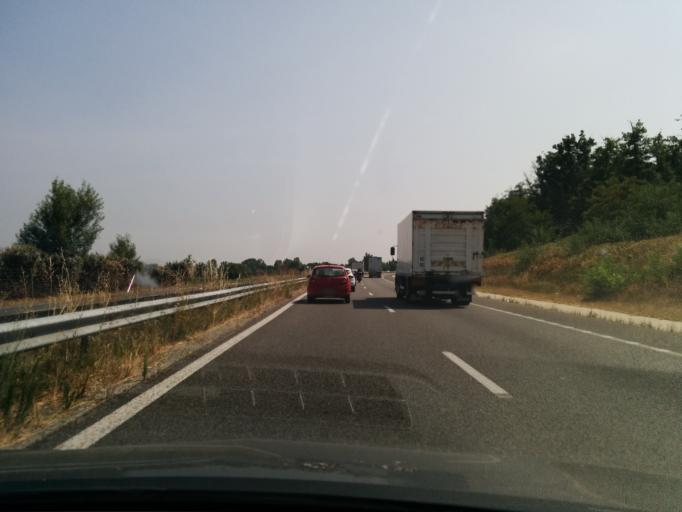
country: FR
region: Midi-Pyrenees
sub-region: Departement du Tarn
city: Giroussens
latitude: 43.8048
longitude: 1.7777
